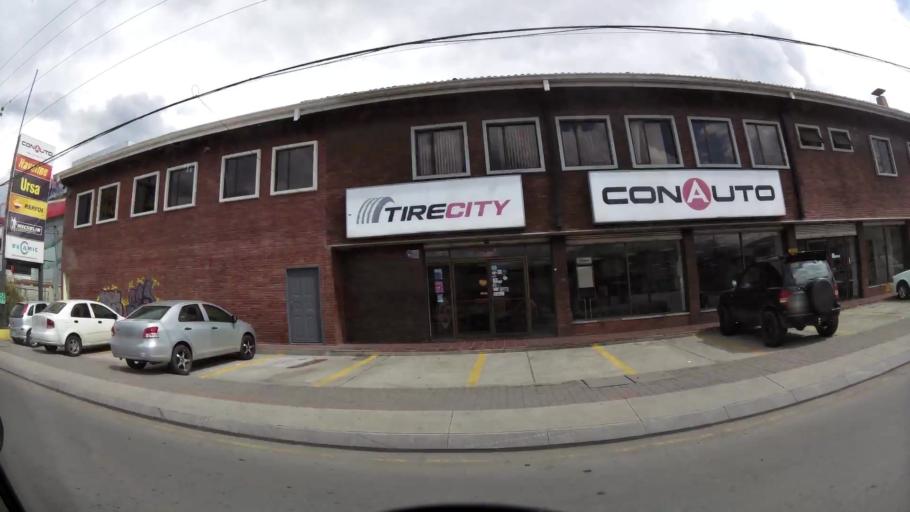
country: EC
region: Azuay
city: Cuenca
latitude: -2.8874
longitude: -78.9851
